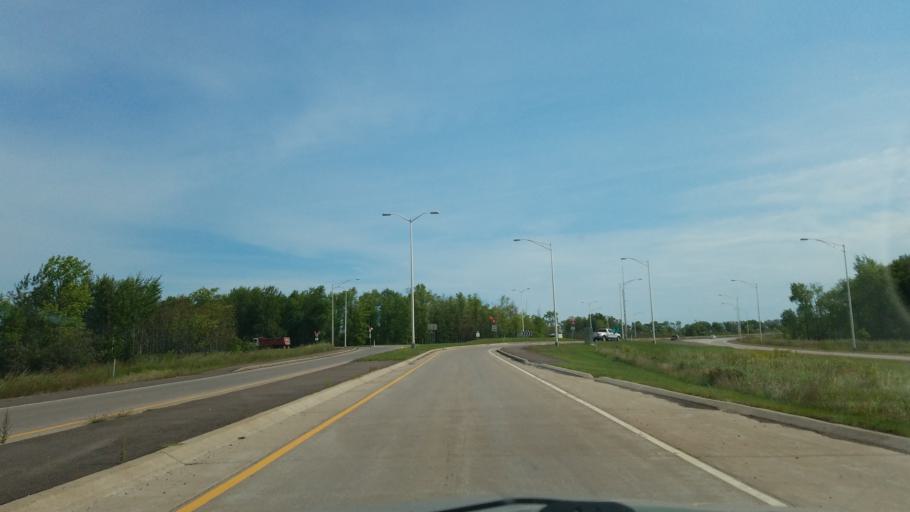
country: US
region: Wisconsin
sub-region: Ashland County
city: Ashland
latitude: 46.5867
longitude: -90.9559
